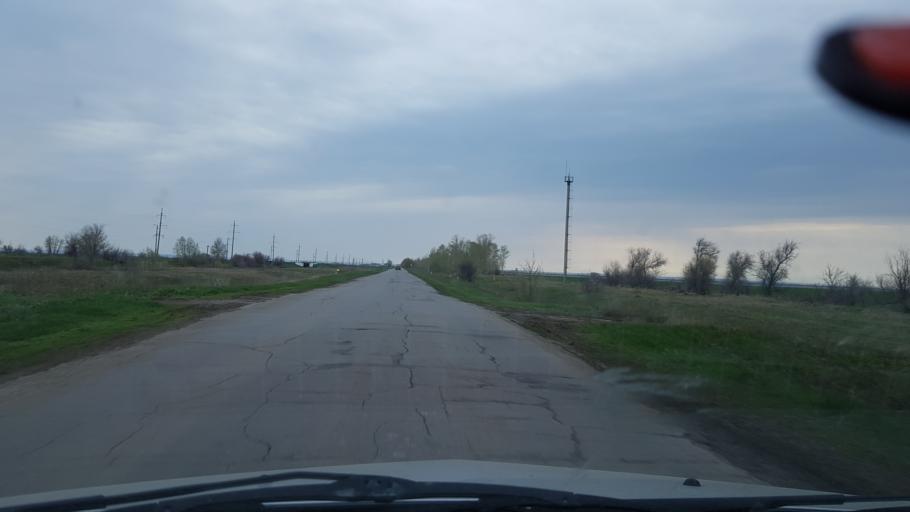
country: RU
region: Samara
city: Khryashchevka
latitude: 53.6689
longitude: 49.1313
